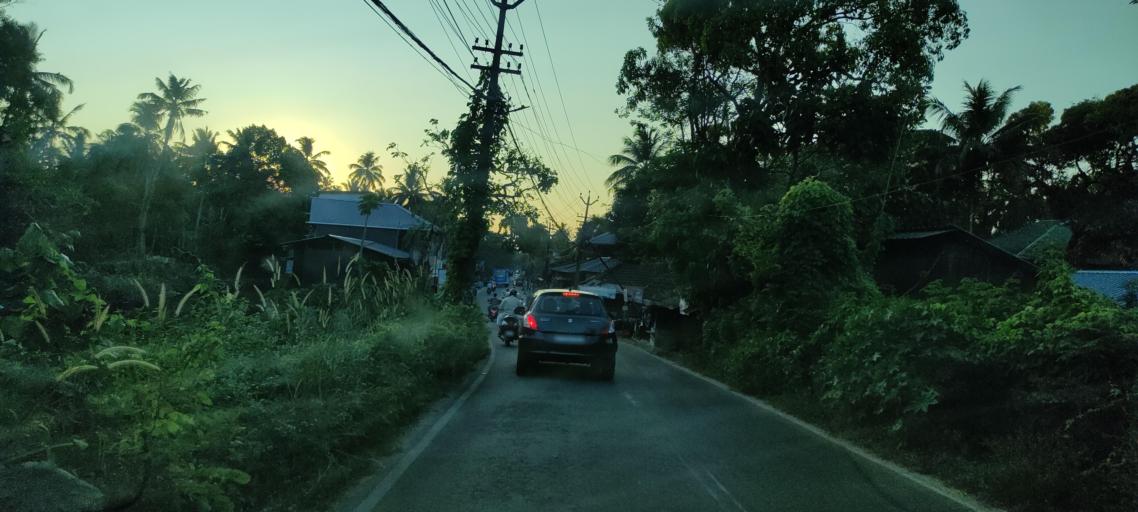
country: IN
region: Kerala
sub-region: Alappuzha
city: Kayankulam
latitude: 9.2601
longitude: 76.4466
